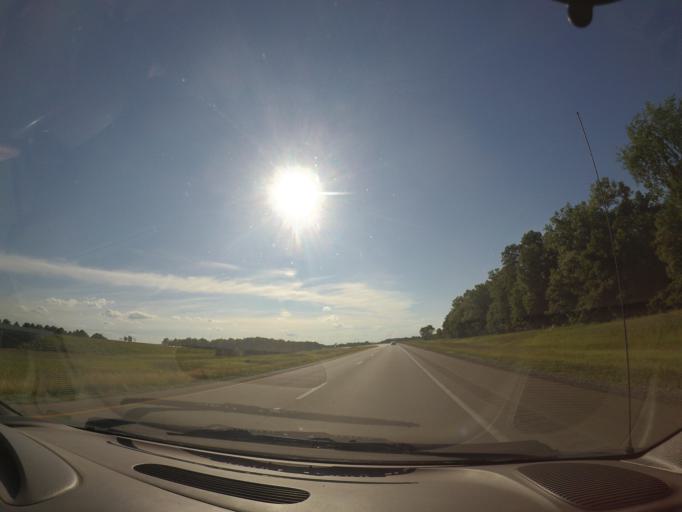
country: US
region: Ohio
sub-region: Henry County
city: Liberty Center
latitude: 41.4162
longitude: -84.0625
